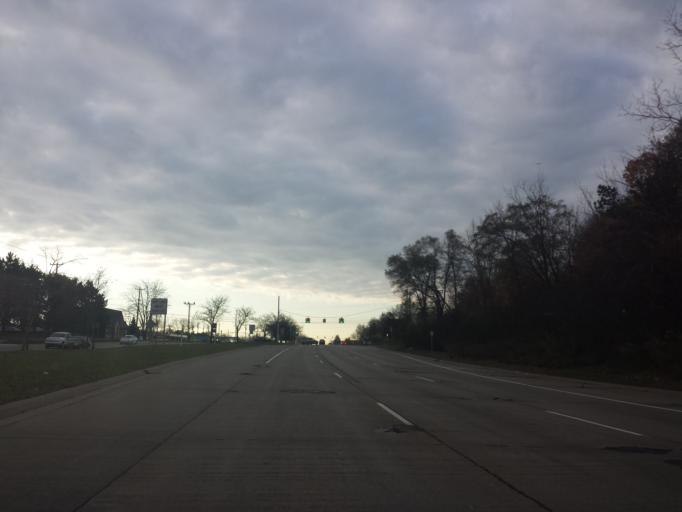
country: US
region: Michigan
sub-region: Oakland County
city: Bloomfield Hills
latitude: 42.5842
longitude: -83.2812
